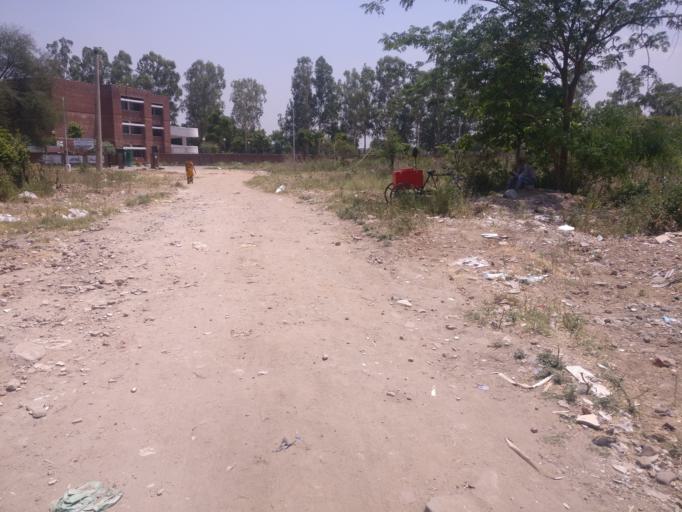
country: IN
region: Punjab
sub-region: Ajitgarh
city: Mohali
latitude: 30.7285
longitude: 76.7287
